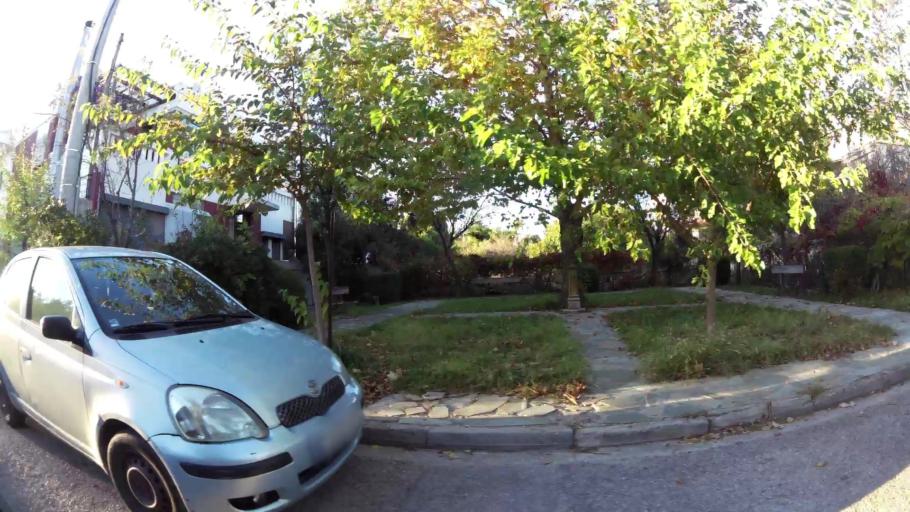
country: GR
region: Attica
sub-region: Nomarchia Anatolikis Attikis
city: Kryoneri
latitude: 38.1338
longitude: 23.8252
